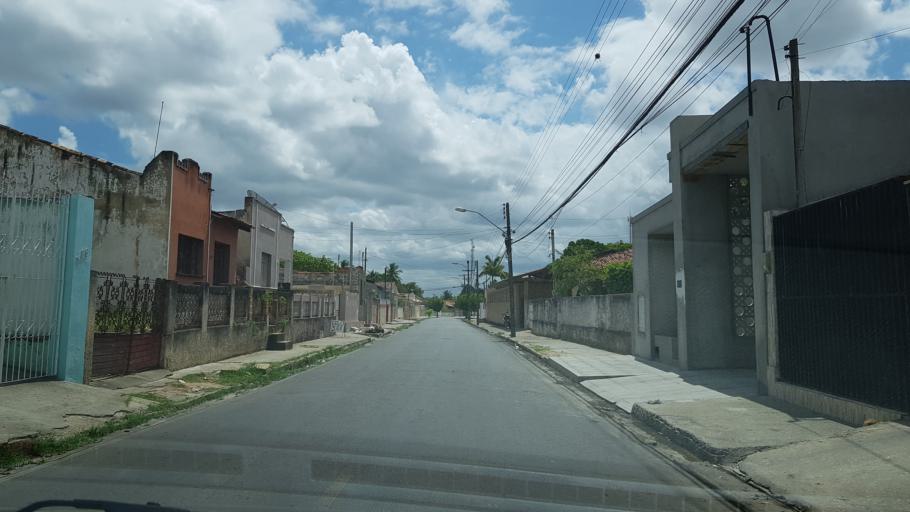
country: BR
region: Alagoas
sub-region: Penedo
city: Penedo
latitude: -10.2798
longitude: -36.5660
